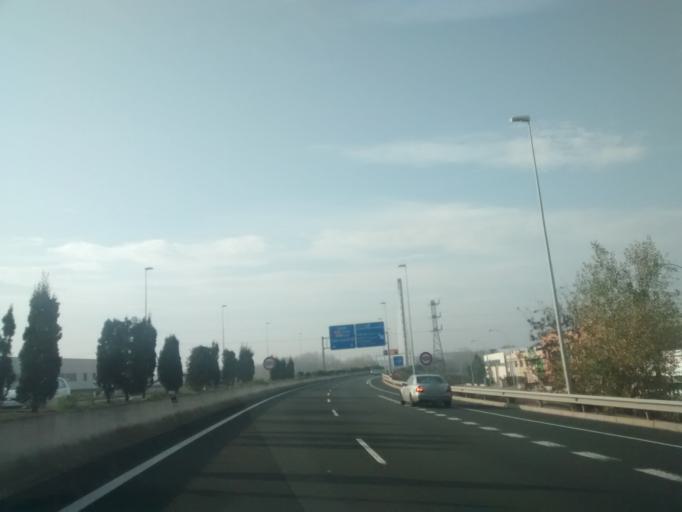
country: ES
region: La Rioja
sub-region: Provincia de La Rioja
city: Villamediana de Iregua
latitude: 42.4558
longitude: -2.4116
